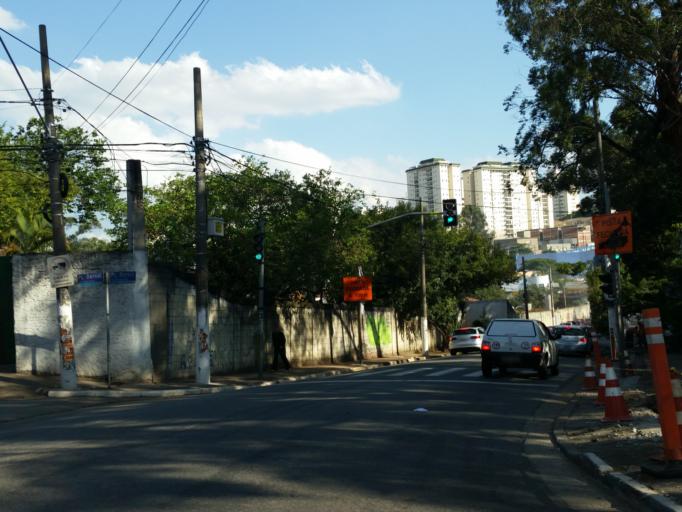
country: BR
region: Sao Paulo
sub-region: Diadema
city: Diadema
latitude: -23.6368
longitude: -46.6613
